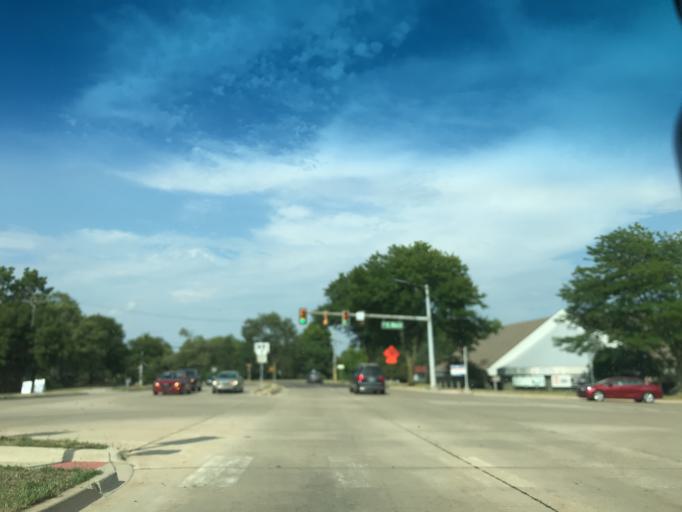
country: US
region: Michigan
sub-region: Washtenaw County
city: Ann Arbor
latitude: 42.2547
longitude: -83.7518
